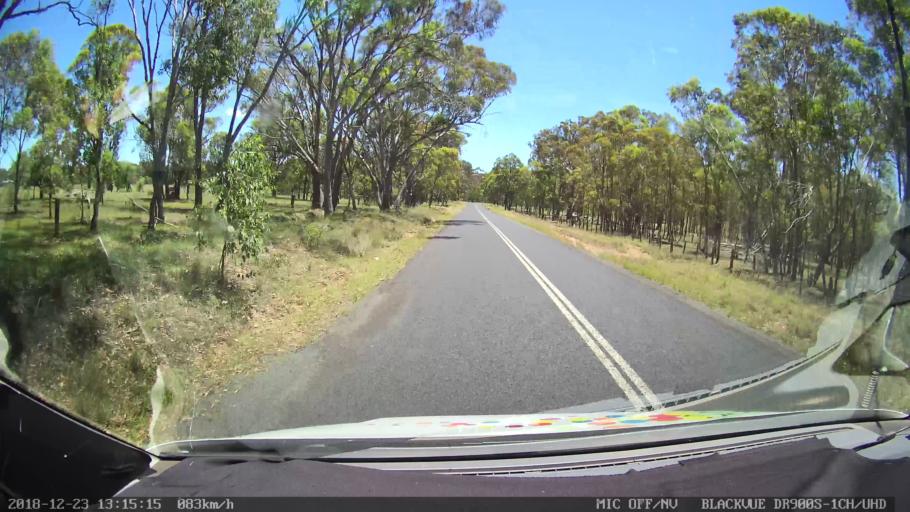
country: AU
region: New South Wales
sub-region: Armidale Dumaresq
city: Armidale
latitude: -30.5034
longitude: 151.5157
